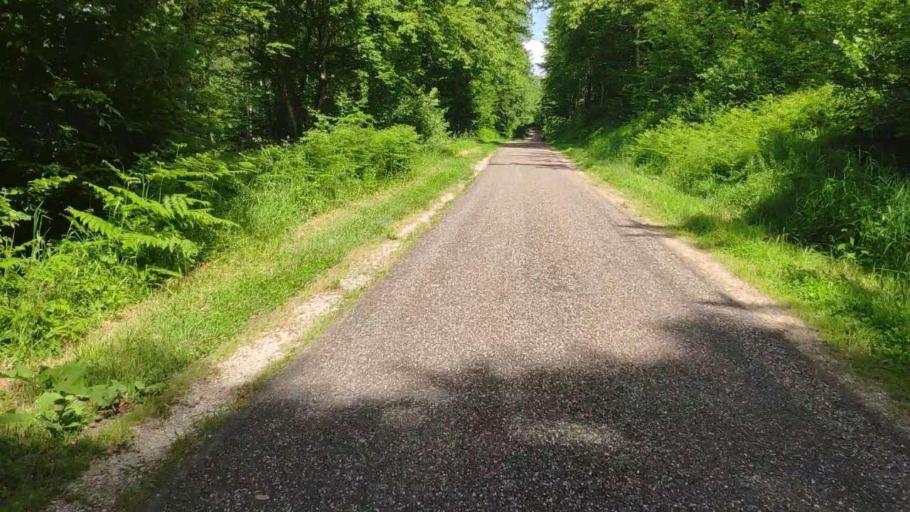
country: FR
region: Franche-Comte
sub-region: Departement du Jura
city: Bletterans
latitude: 46.7201
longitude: 5.4831
